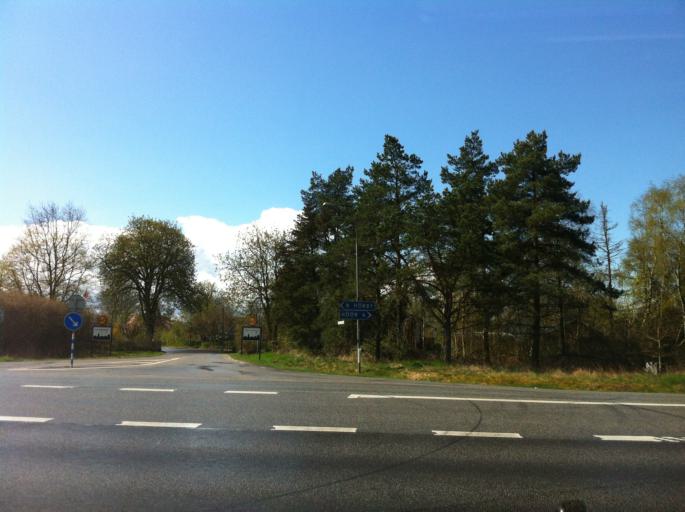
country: SE
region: Skane
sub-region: Hoors Kommun
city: Satofta
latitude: 55.9055
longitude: 13.6089
